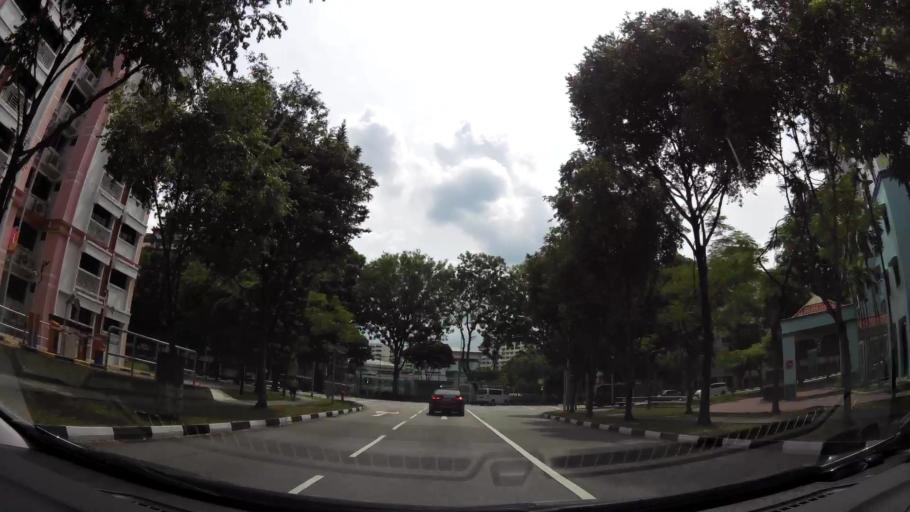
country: MY
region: Johor
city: Johor Bahru
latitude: 1.4015
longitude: 103.7457
